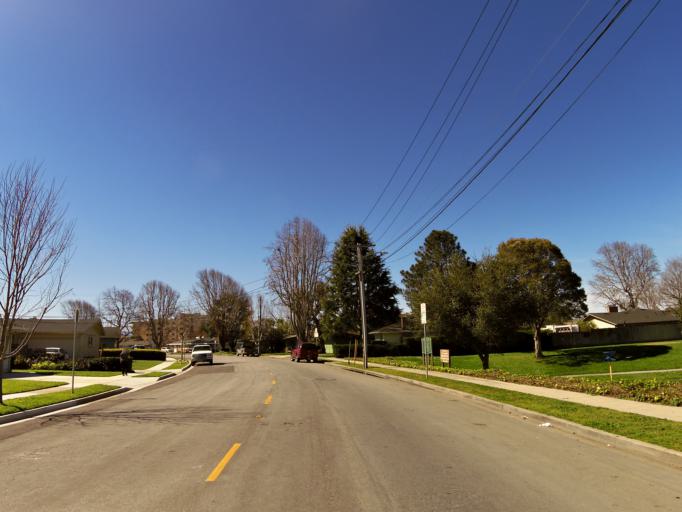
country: US
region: California
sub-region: Monterey County
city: Salinas
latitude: 36.6615
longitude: -121.6436
